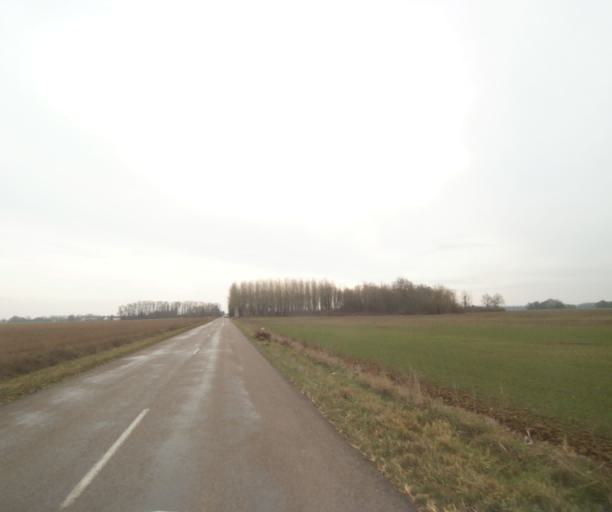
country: FR
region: Champagne-Ardenne
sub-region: Departement de la Haute-Marne
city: Villiers-en-Lieu
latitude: 48.6762
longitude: 4.8879
